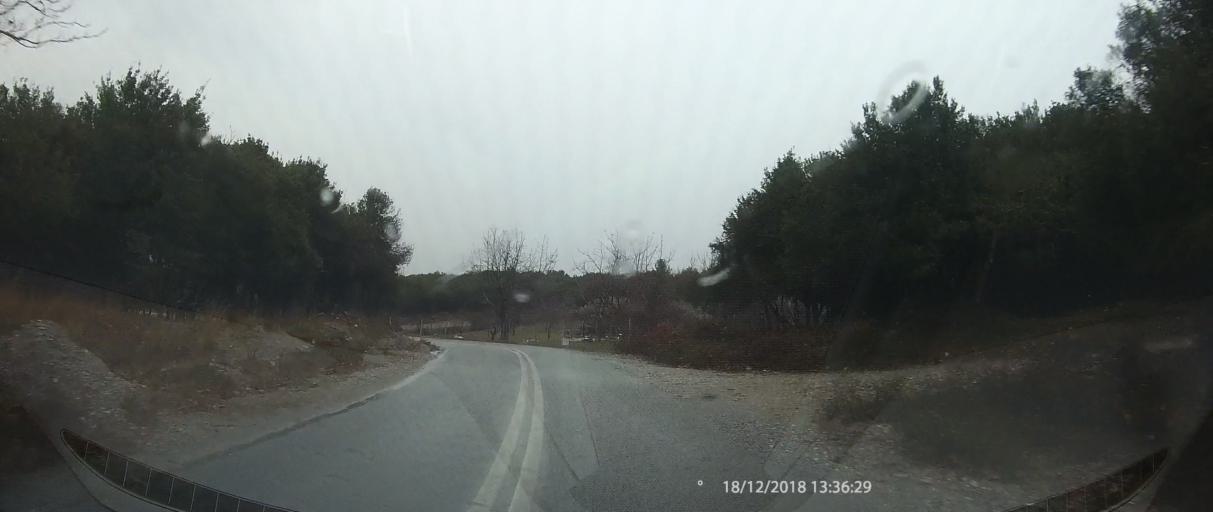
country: GR
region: Central Macedonia
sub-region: Nomos Pierias
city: Litochoro
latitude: 40.1106
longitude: 22.4937
